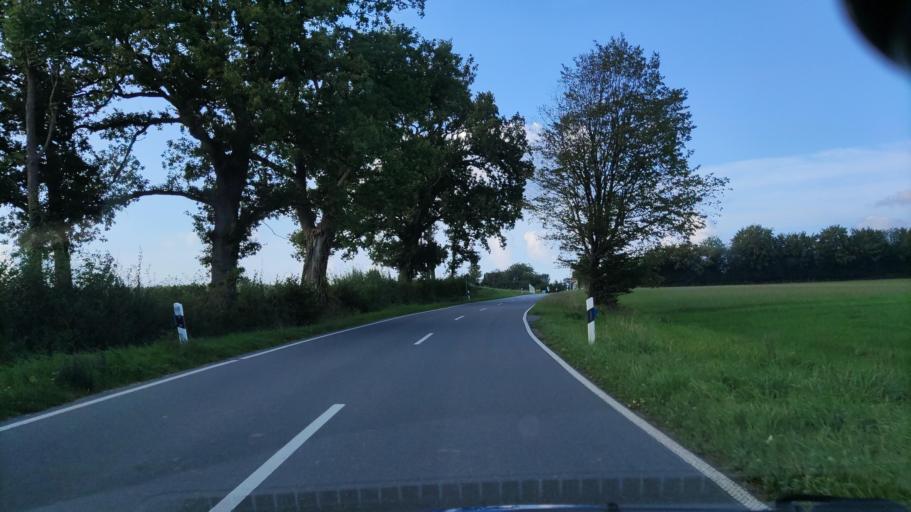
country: DE
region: Schleswig-Holstein
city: Glasau
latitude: 54.0473
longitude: 10.5306
